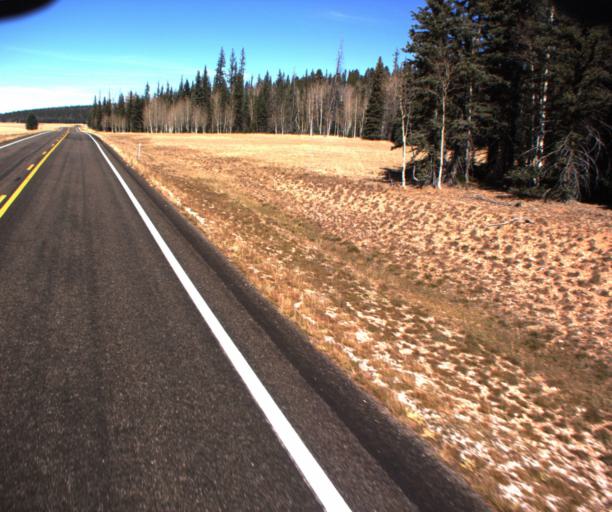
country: US
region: Arizona
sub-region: Coconino County
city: Grand Canyon
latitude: 36.3472
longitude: -112.1176
